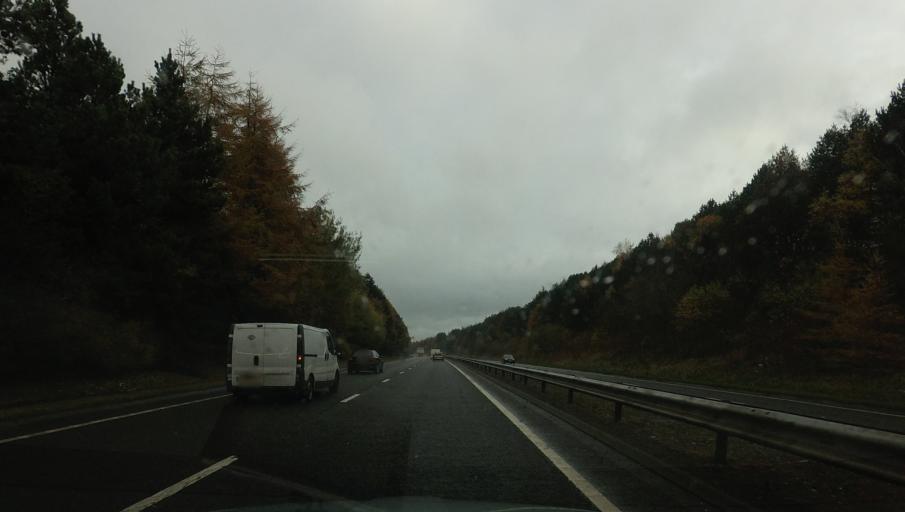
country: GB
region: Scotland
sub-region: Fife
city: Cardenden
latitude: 56.1268
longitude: -3.2640
